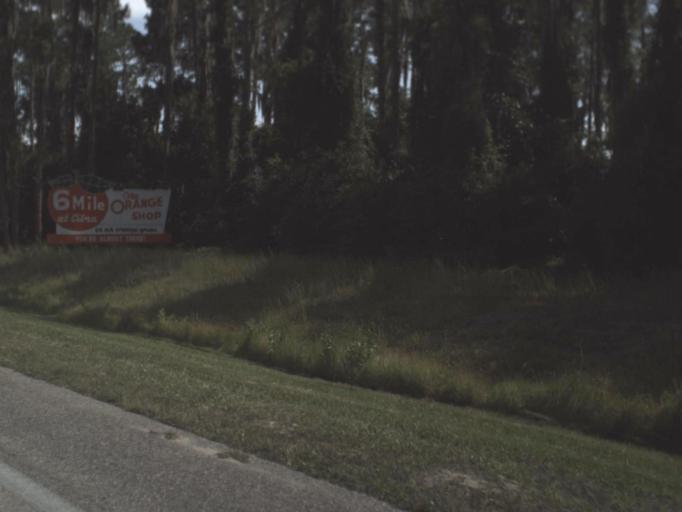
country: US
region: Florida
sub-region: Alachua County
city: Hawthorne
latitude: 29.5080
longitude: -82.0999
